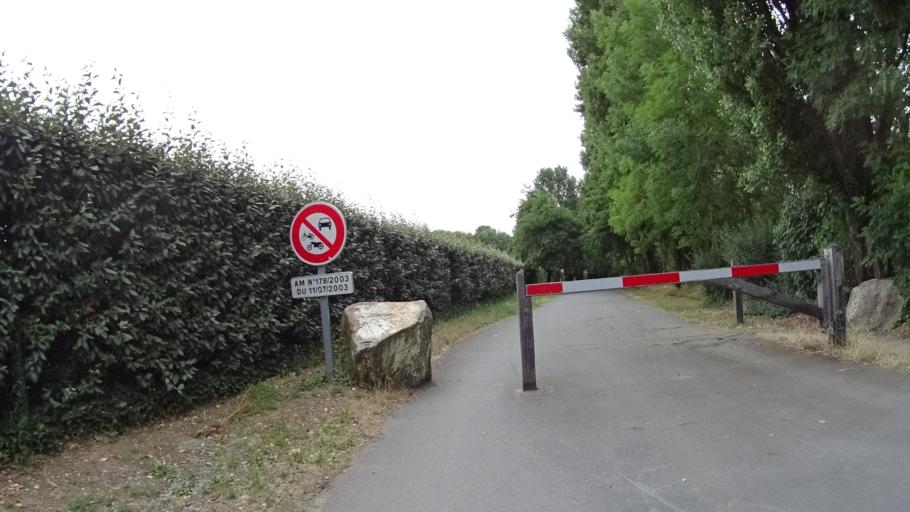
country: FR
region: Pays de la Loire
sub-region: Departement de la Loire-Atlantique
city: Sainte-Luce-sur-Loire
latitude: 47.2451
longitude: -1.4611
